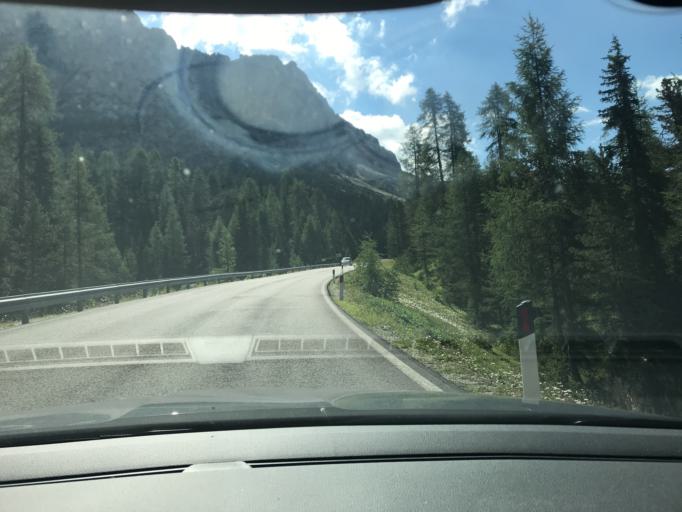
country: IT
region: Veneto
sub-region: Provincia di Belluno
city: Livinallongo del Col di Lana
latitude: 46.5413
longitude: 11.9815
